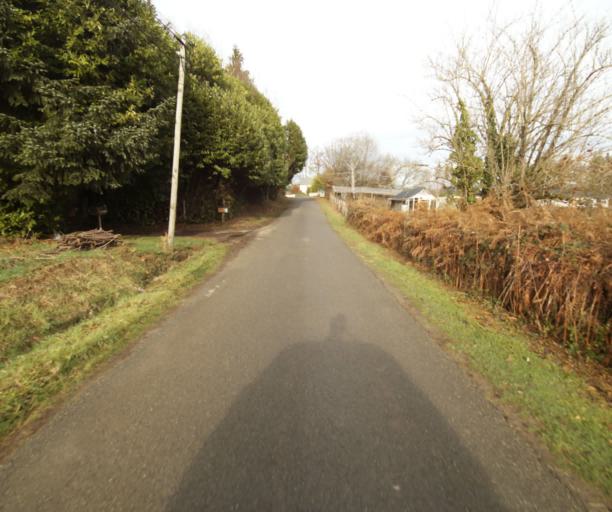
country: FR
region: Limousin
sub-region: Departement de la Correze
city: Saint-Mexant
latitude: 45.2801
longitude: 1.6873
